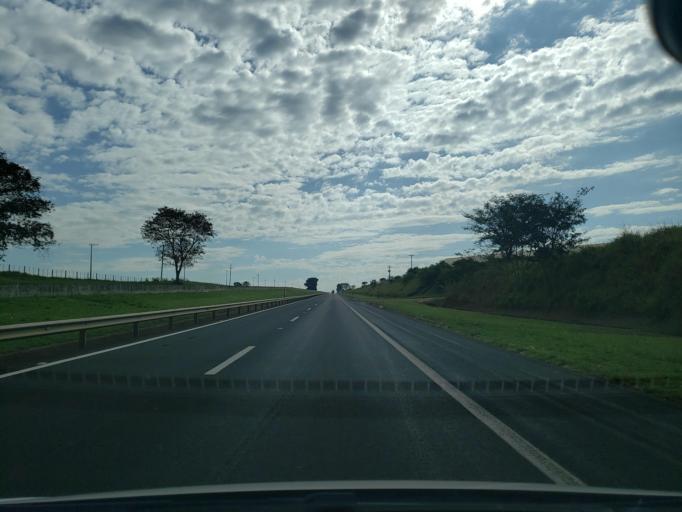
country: BR
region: Sao Paulo
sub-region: Lins
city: Lins
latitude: -21.6453
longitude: -49.8190
